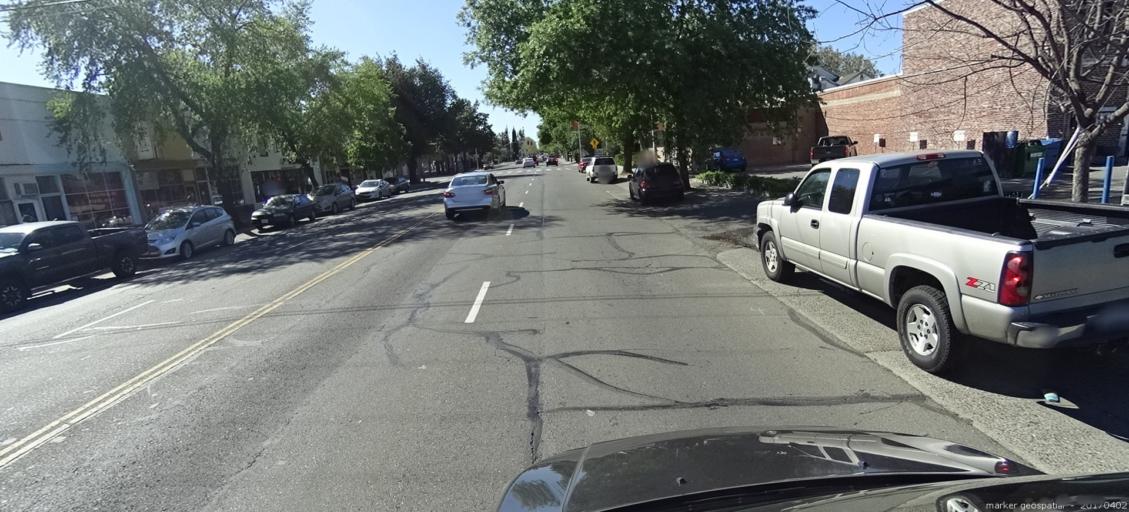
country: US
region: California
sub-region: Sacramento County
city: Sacramento
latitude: 38.5611
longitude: -121.4902
